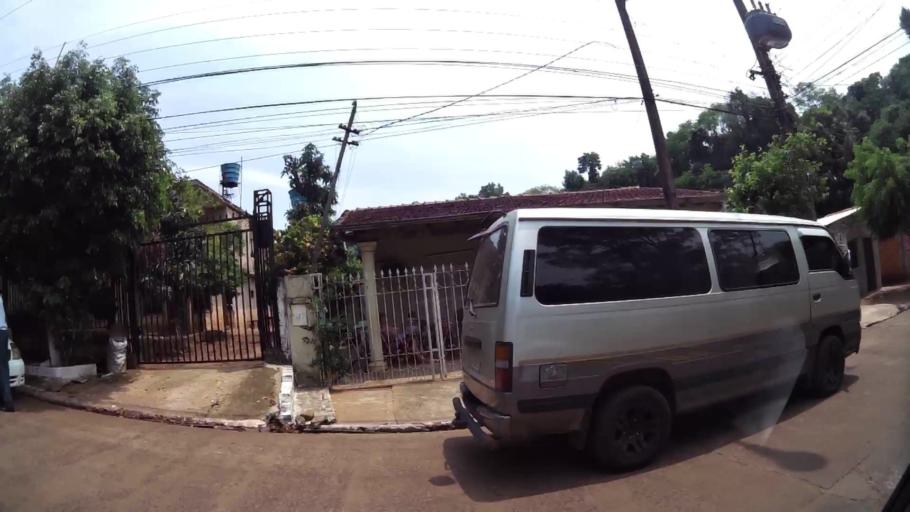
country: PY
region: Alto Parana
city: Ciudad del Este
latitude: -25.5039
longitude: -54.6158
